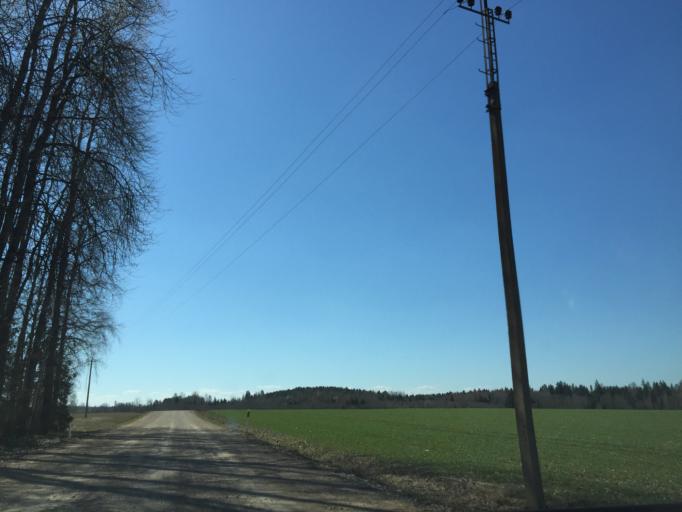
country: EE
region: Viljandimaa
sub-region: Viiratsi vald
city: Viiratsi
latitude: 58.3376
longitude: 25.7141
